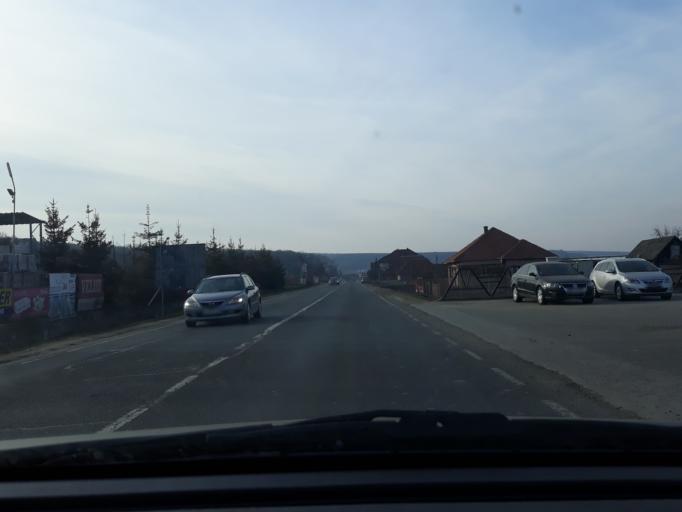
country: RO
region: Salaj
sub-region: Comuna Hereclean
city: Hereclean
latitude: 47.2247
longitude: 23.0183
